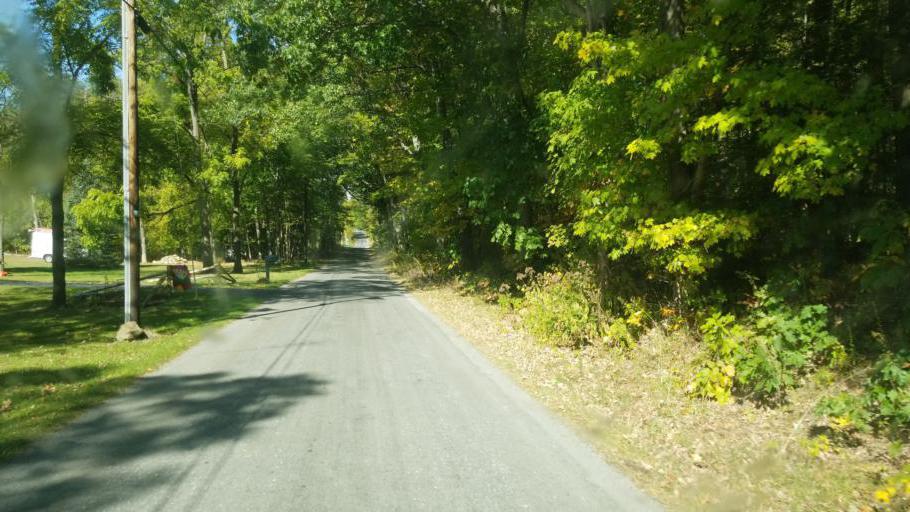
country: US
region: Pennsylvania
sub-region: Mercer County
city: Mercer
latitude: 41.3363
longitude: -80.2456
